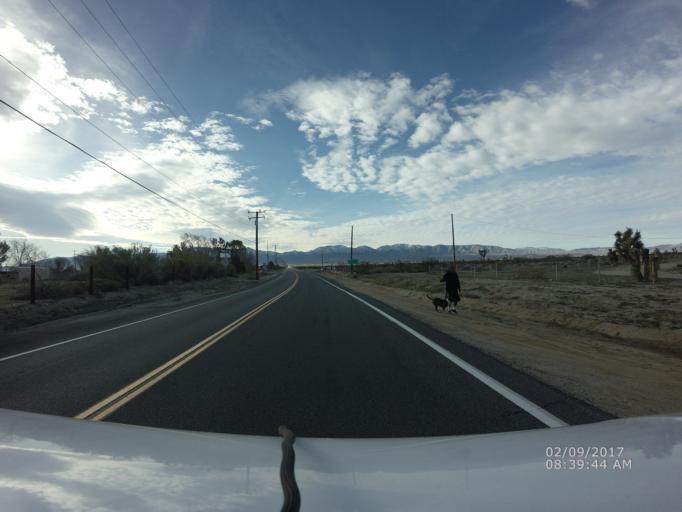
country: US
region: California
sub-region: Los Angeles County
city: Lake Los Angeles
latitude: 34.5436
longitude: -117.8356
